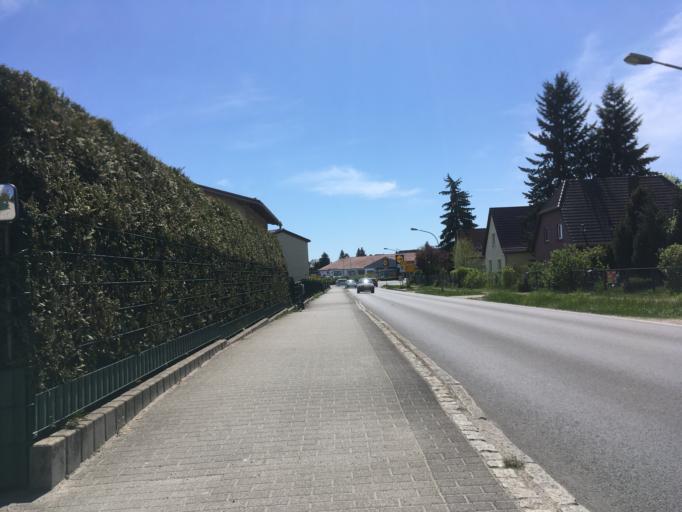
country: DE
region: Brandenburg
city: Wildau
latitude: 52.3242
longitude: 13.6145
